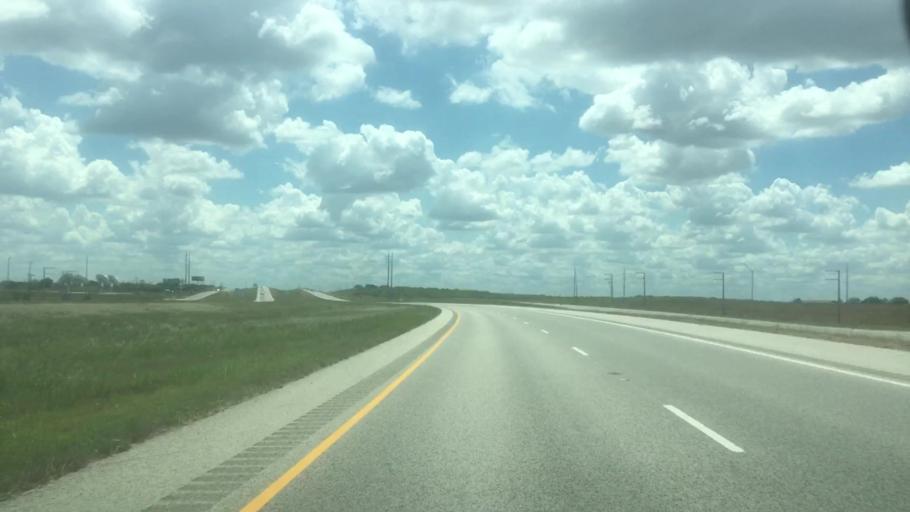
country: US
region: Texas
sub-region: Caldwell County
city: Uhland
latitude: 30.0168
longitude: -97.6881
